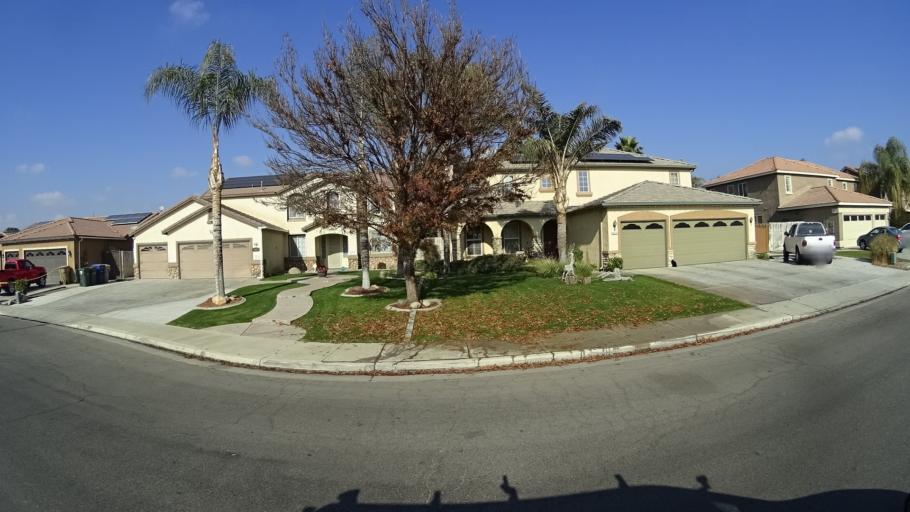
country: US
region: California
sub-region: Kern County
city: Greenacres
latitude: 35.3019
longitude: -119.1078
